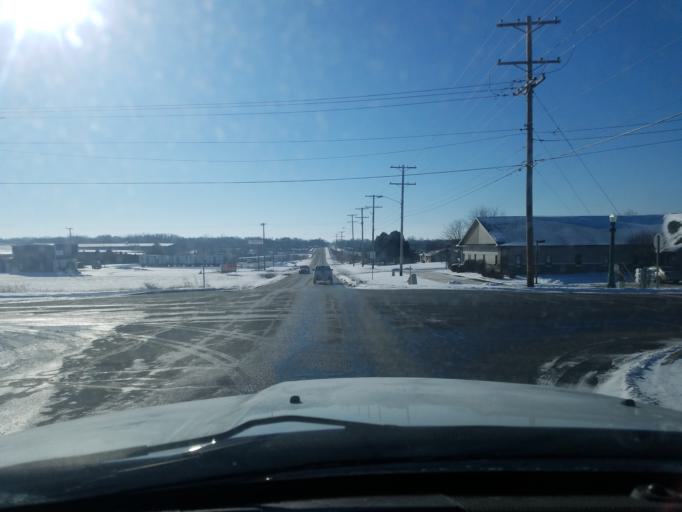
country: US
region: Indiana
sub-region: Noble County
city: Kendallville
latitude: 41.4450
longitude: -85.2318
